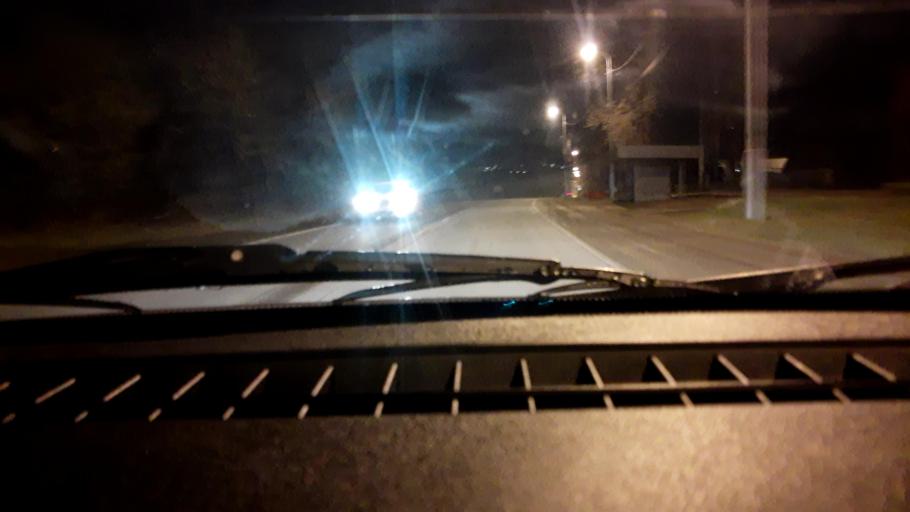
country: RU
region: Bashkortostan
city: Blagoveshchensk
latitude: 54.8949
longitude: 56.0543
